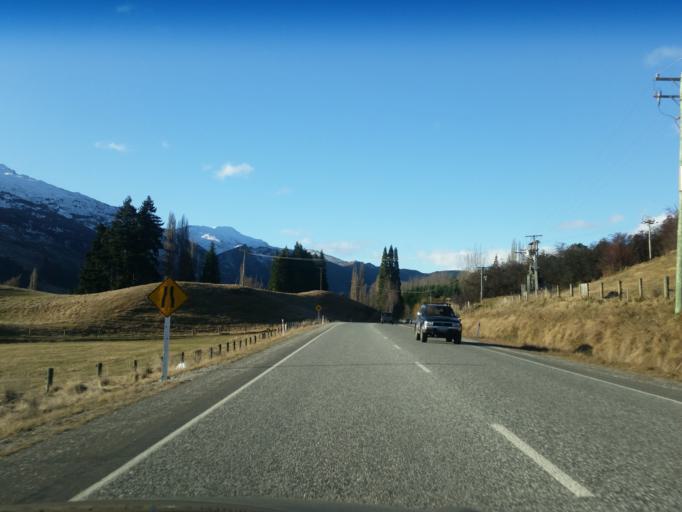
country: NZ
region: Otago
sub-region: Queenstown-Lakes District
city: Queenstown
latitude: -44.9620
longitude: 168.7202
